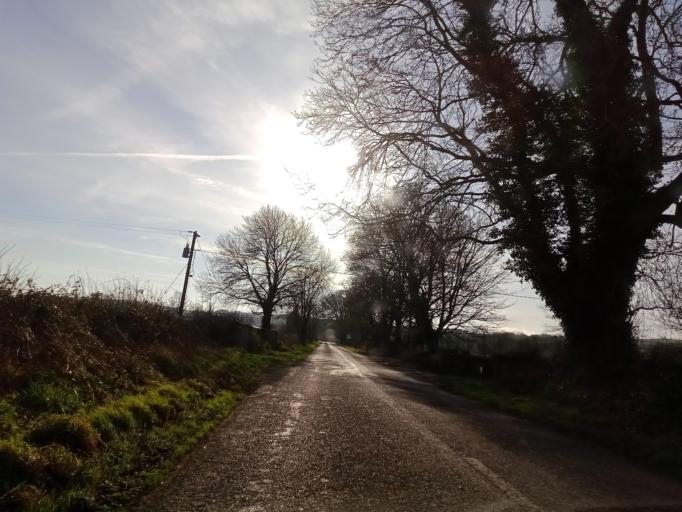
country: IE
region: Munster
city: Fethard
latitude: 52.5648
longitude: -7.5637
